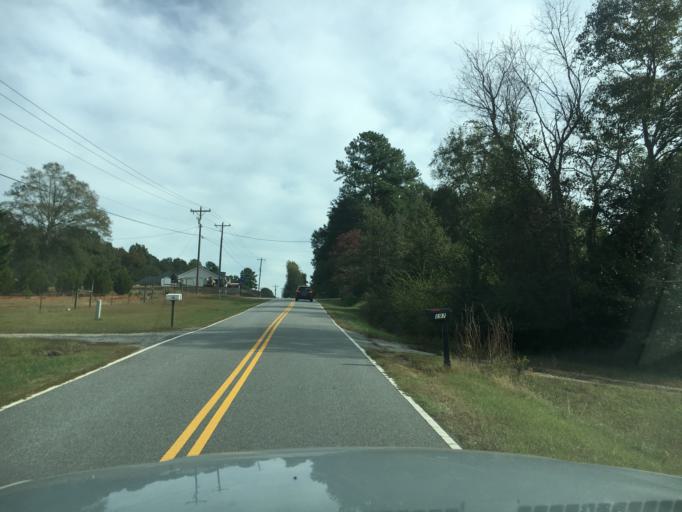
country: US
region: South Carolina
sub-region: Spartanburg County
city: Duncan
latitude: 34.9145
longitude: -82.1374
